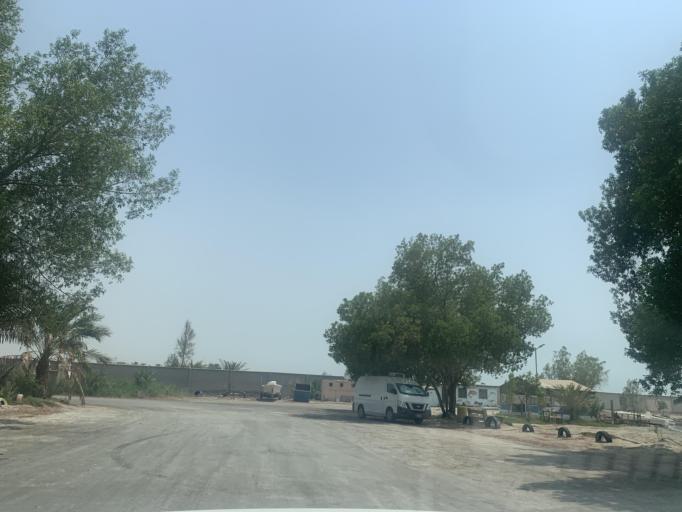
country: BH
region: Central Governorate
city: Madinat Hamad
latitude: 26.1228
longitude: 50.4620
